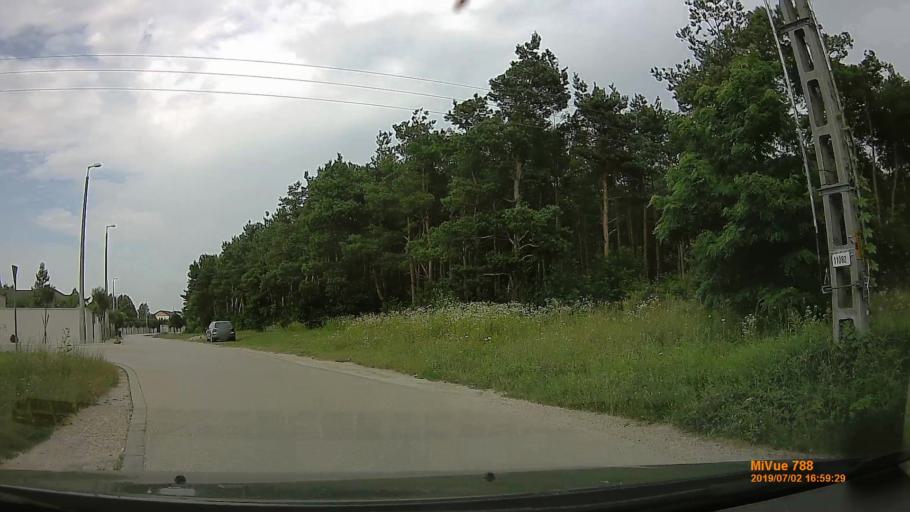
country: HU
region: Gyor-Moson-Sopron
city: Mosonmagyarovar
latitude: 47.8868
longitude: 17.2855
